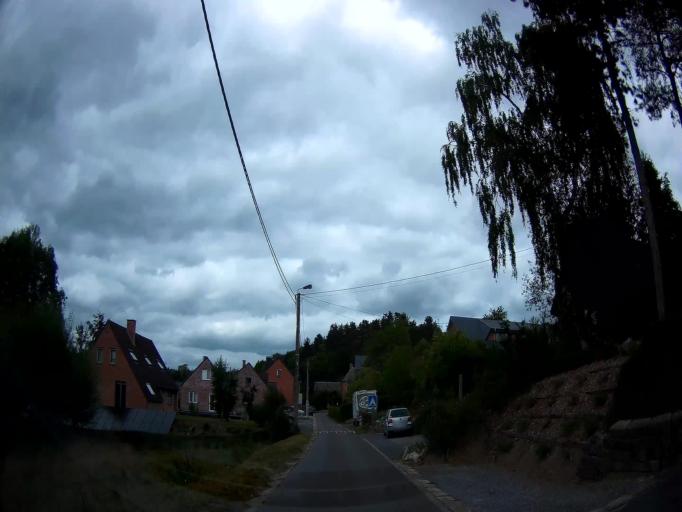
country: BE
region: Wallonia
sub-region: Province de Namur
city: Rochefort
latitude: 50.1623
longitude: 5.2275
